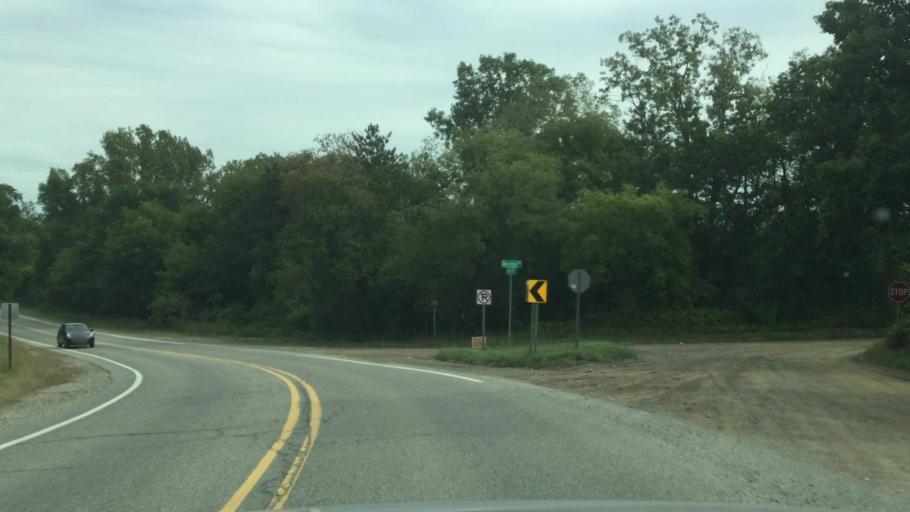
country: US
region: Michigan
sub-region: Oakland County
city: Holly
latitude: 42.8147
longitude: -83.5601
